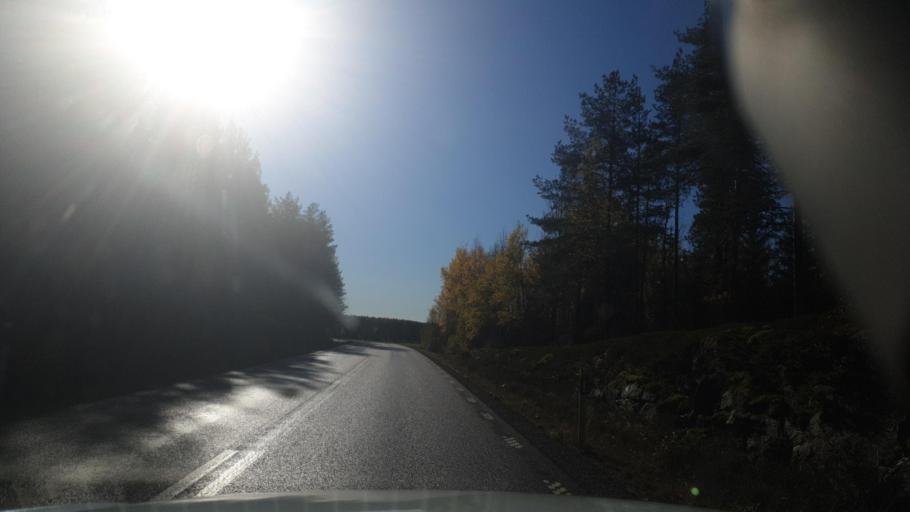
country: SE
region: Vaermland
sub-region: Arvika Kommun
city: Arvika
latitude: 59.4900
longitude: 12.7606
